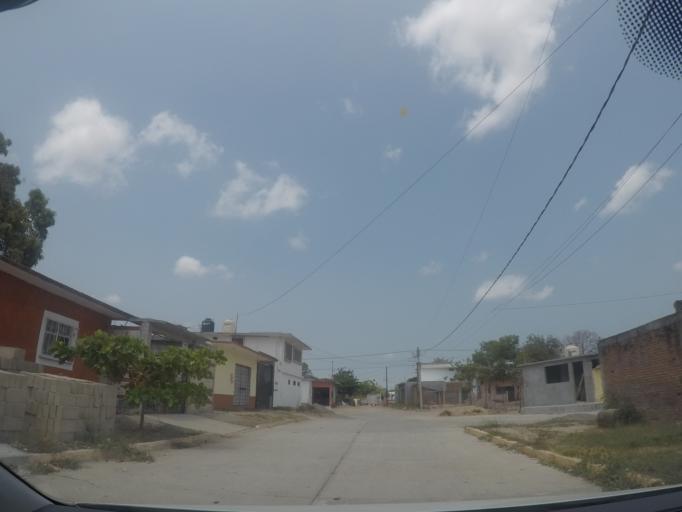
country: MX
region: Oaxaca
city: Asuncion Ixtaltepec
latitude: 16.4998
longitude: -95.0613
